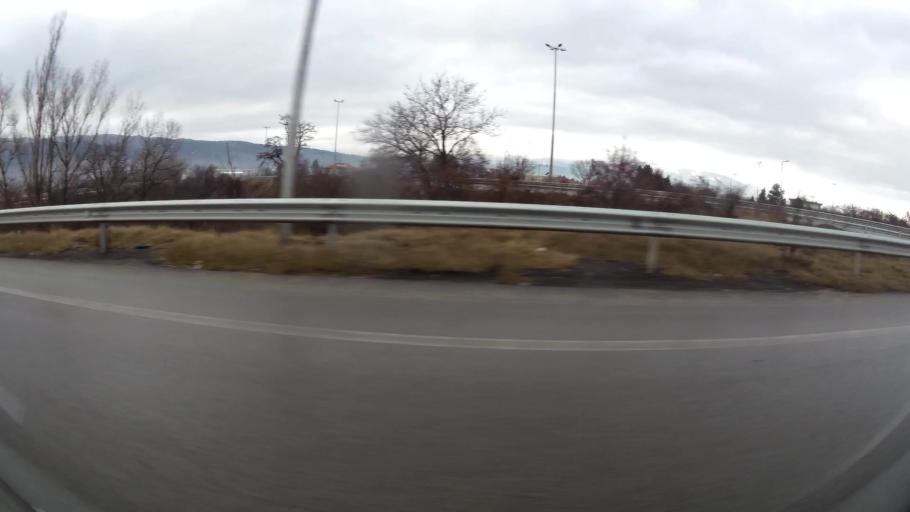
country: BG
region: Sofia-Capital
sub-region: Stolichna Obshtina
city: Sofia
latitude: 42.6320
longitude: 23.4482
